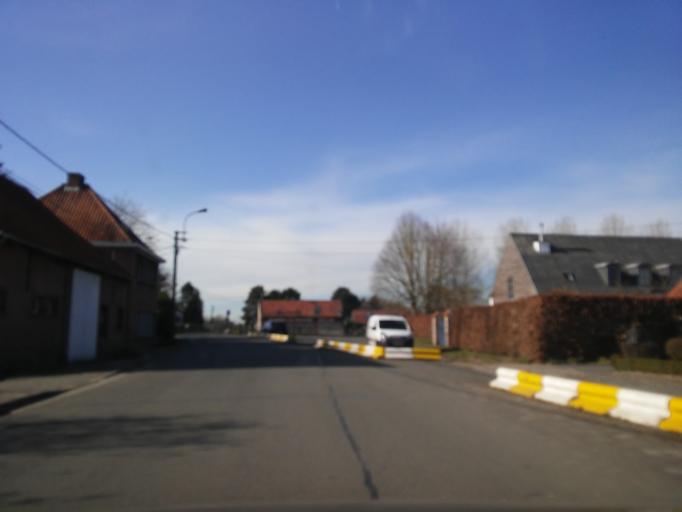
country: BE
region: Flanders
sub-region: Provincie Oost-Vlaanderen
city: Eeklo
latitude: 51.1897
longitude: 3.5276
